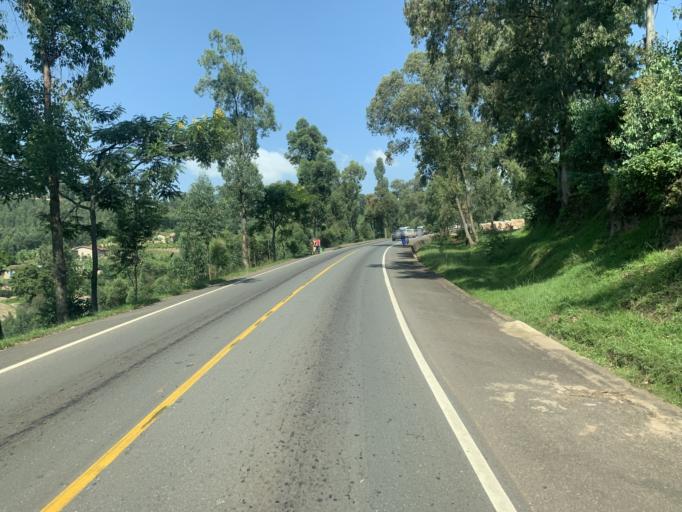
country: RW
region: Kigali
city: Kigali
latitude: -1.9929
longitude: 29.9216
